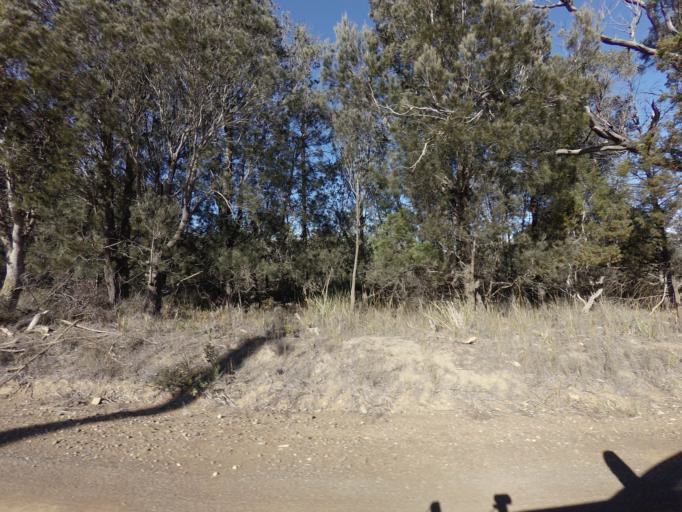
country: AU
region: Tasmania
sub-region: Sorell
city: Sorell
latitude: -42.3541
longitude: 147.9674
